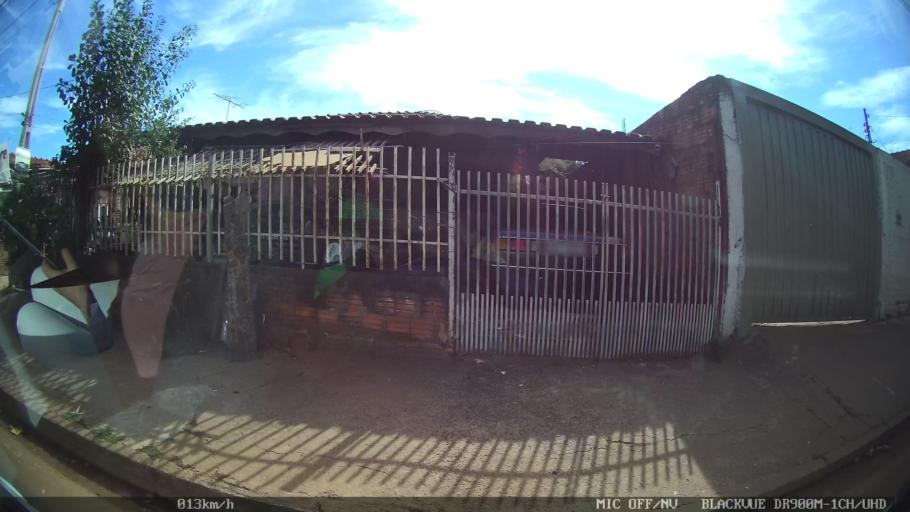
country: BR
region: Sao Paulo
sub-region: Sao Jose Do Rio Preto
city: Sao Jose do Rio Preto
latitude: -20.8415
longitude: -49.3341
